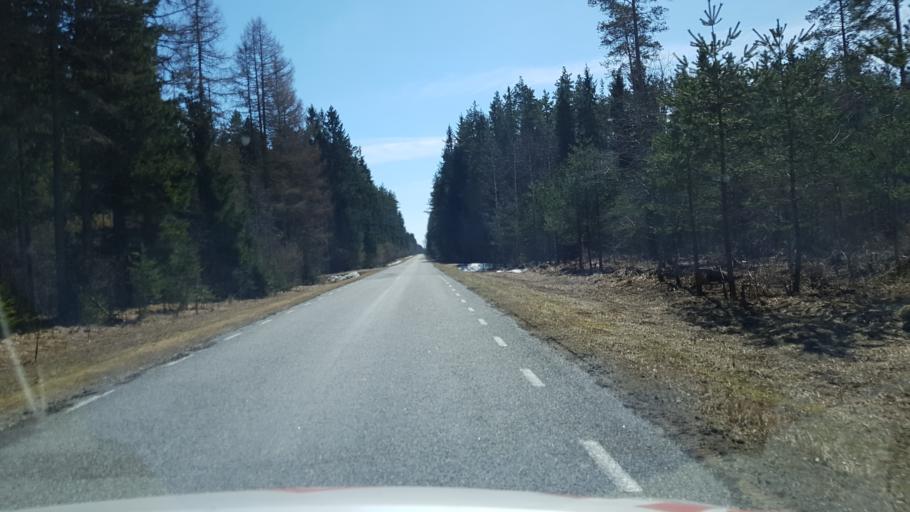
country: EE
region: Laeaene-Virumaa
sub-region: Vinni vald
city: Vinni
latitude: 59.1569
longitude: 26.5151
